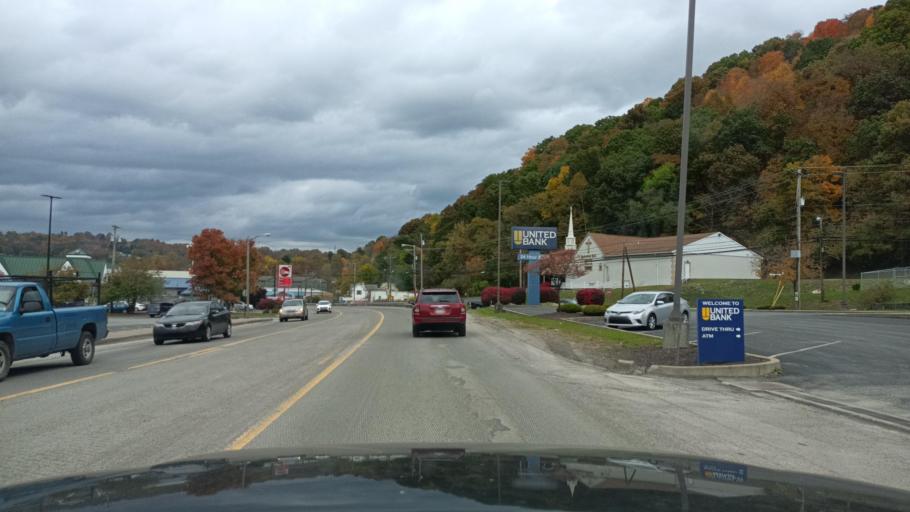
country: US
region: West Virginia
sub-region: Monongalia County
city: Brookhaven
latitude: 39.6234
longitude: -79.9241
